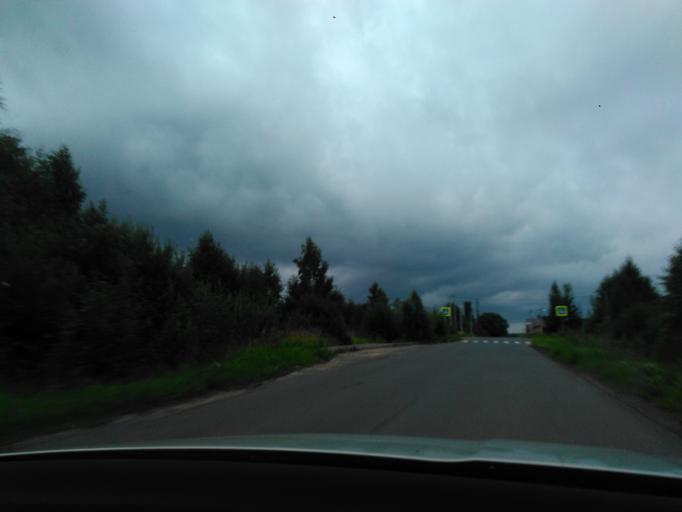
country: RU
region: Tverskaya
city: Konakovo
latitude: 56.6730
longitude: 36.7124
